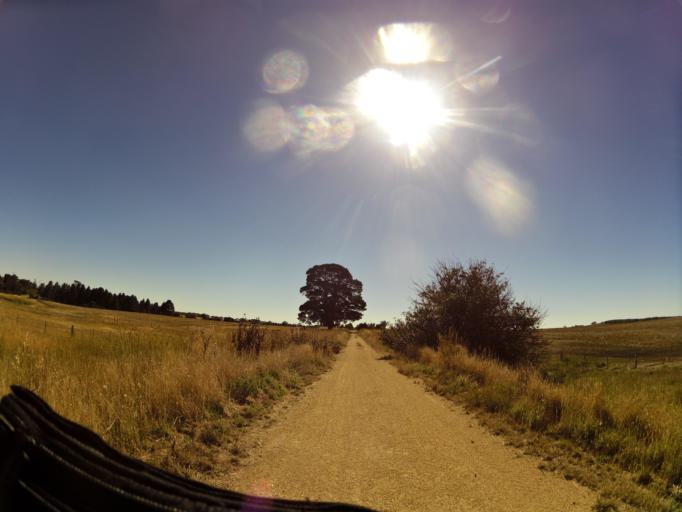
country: AU
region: Victoria
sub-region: Ballarat North
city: Delacombe
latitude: -37.6845
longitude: 143.4113
